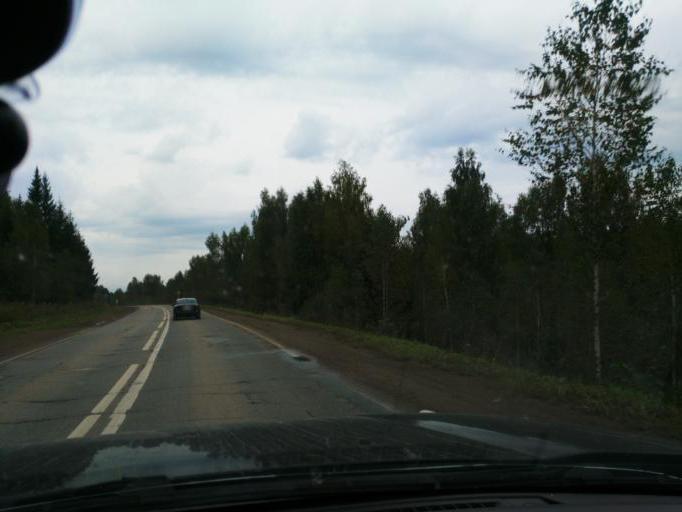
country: RU
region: Perm
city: Chernushka
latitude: 56.6817
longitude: 56.1771
